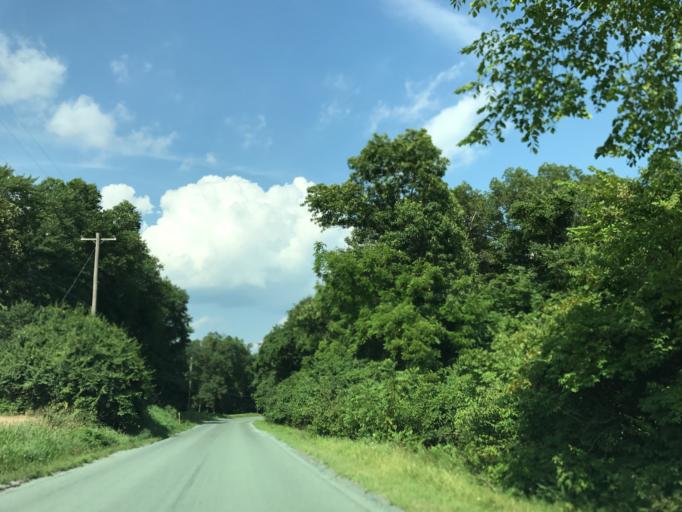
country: US
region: Pennsylvania
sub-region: York County
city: Pennville
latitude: 39.7554
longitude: -76.9974
